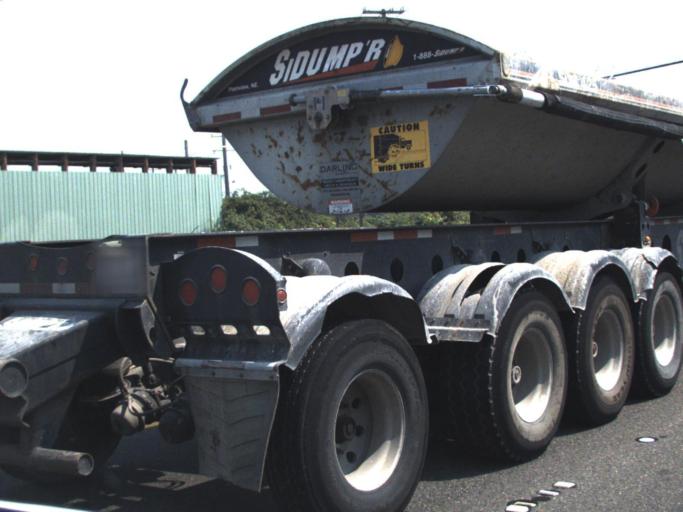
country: US
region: Washington
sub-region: King County
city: White Center
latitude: 47.5322
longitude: -122.3304
